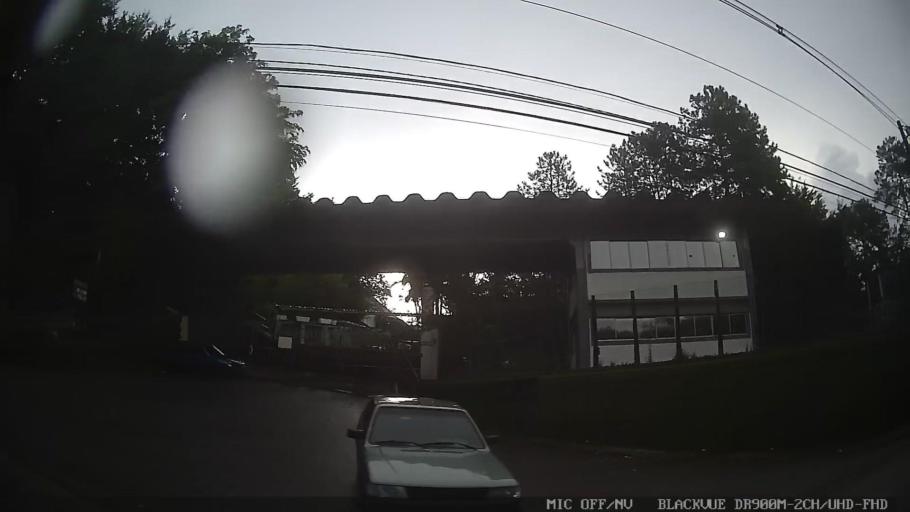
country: BR
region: Sao Paulo
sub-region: Ribeirao Pires
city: Ribeirao Pires
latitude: -23.7091
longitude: -46.3772
